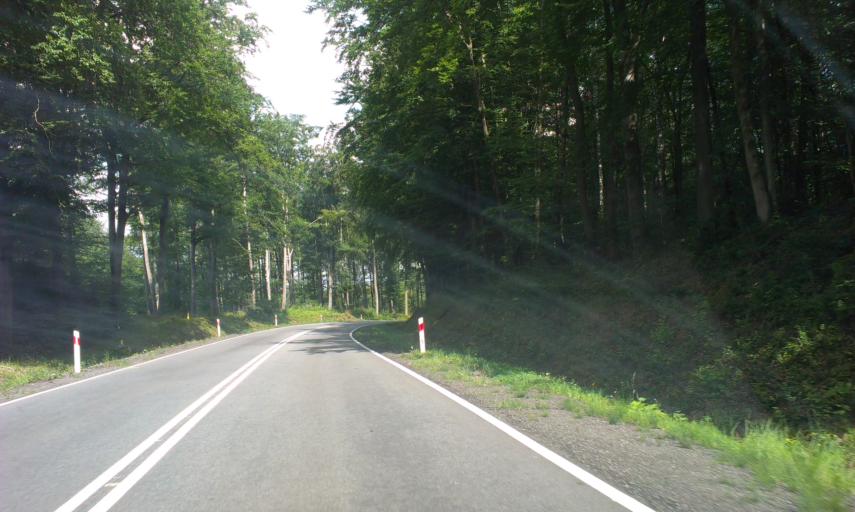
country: PL
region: West Pomeranian Voivodeship
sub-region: Powiat koszalinski
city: Bobolice
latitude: 53.9224
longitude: 16.6019
